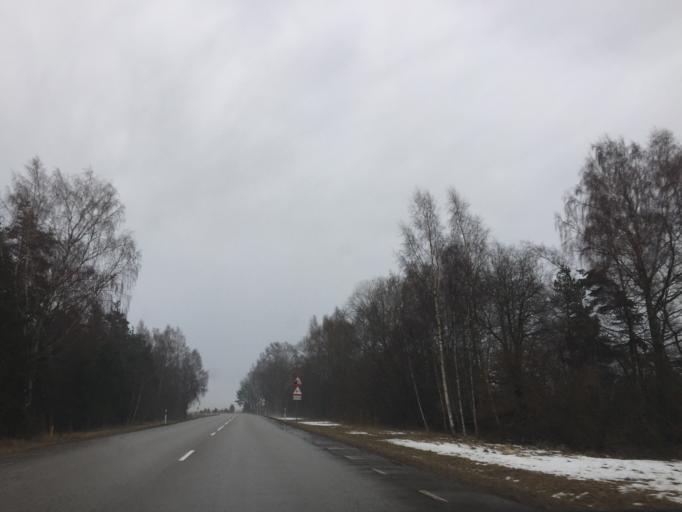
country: EE
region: Saare
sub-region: Orissaare vald
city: Orissaare
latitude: 58.5493
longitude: 23.1207
